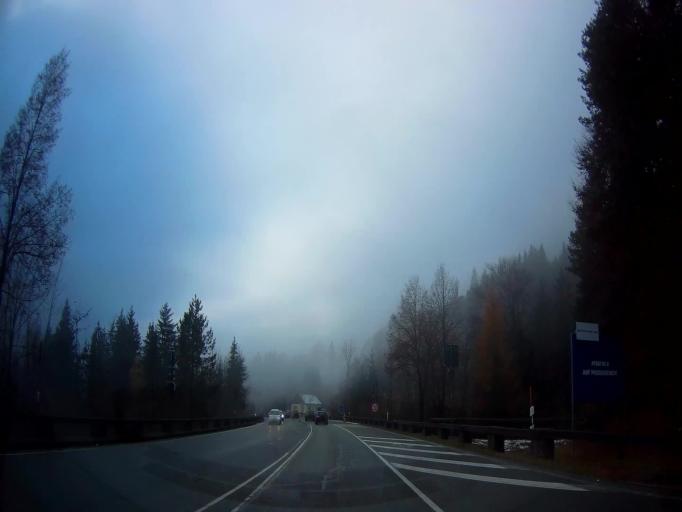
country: AT
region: Salzburg
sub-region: Politischer Bezirk Zell am See
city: Unken
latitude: 47.6679
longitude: 12.7566
